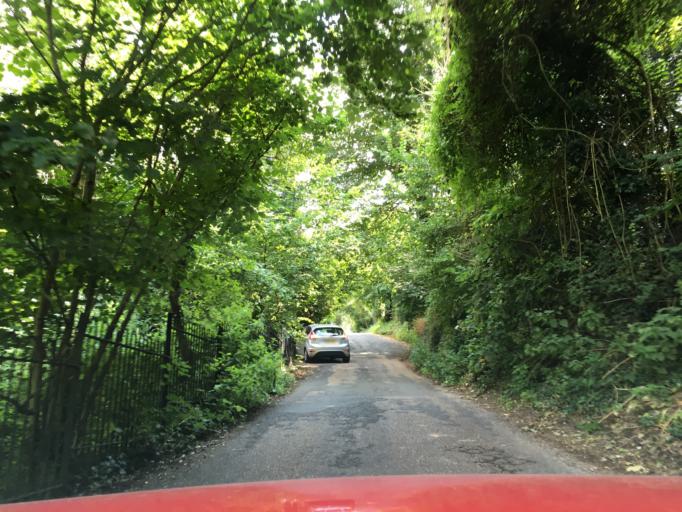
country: GB
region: England
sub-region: Kent
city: Maidstone
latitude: 51.2388
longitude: 0.5215
